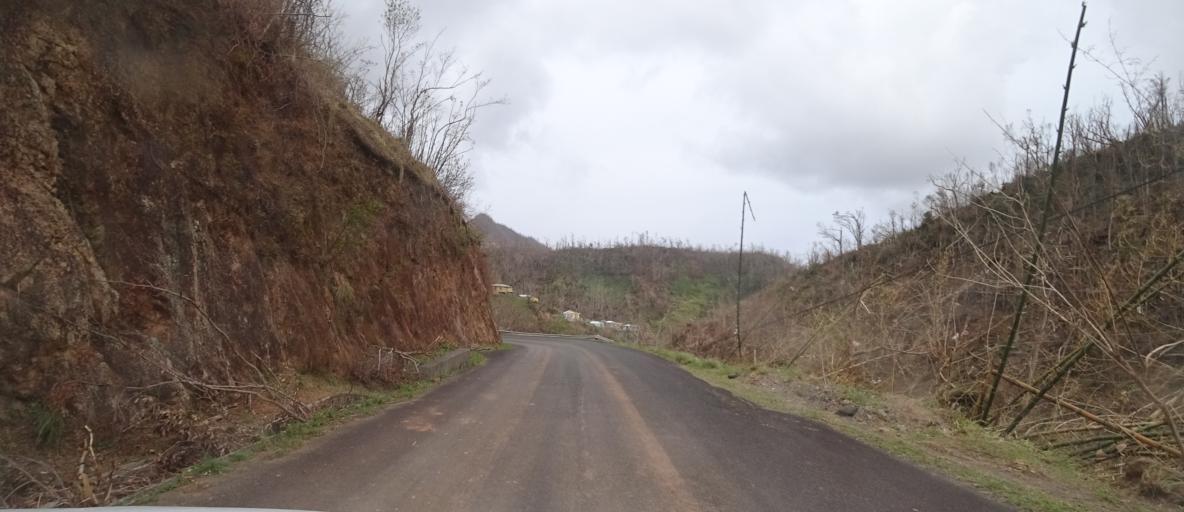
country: DM
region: Saint John
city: Portsmouth
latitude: 15.5826
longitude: -61.4154
